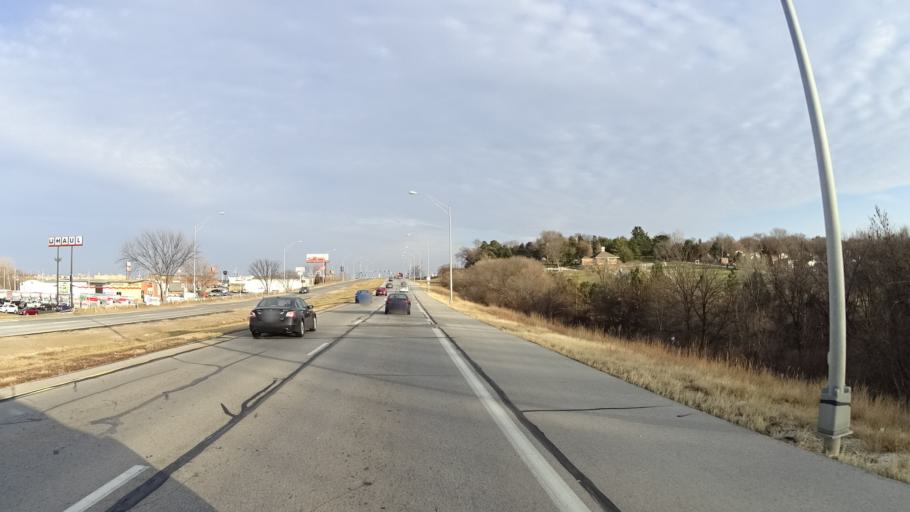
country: US
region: Nebraska
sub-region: Douglas County
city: Ralston
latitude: 41.2124
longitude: -96.0486
